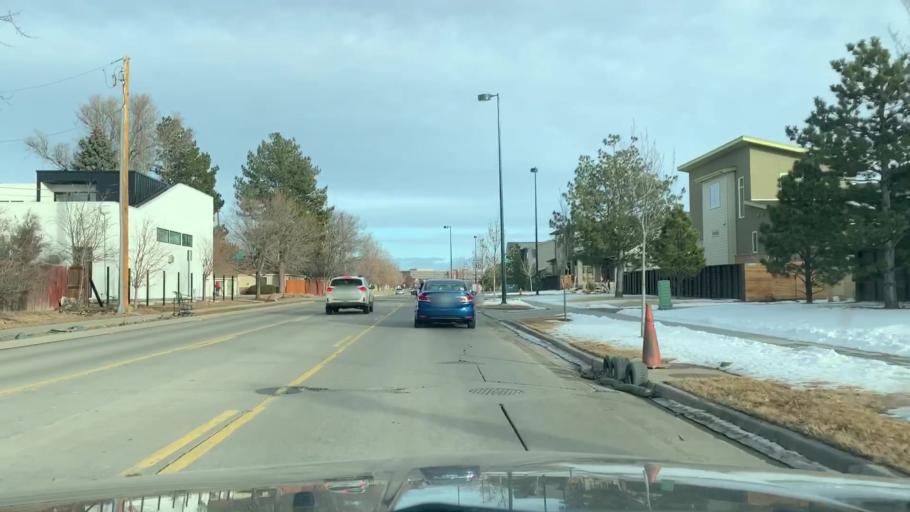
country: US
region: Colorado
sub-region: Arapahoe County
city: Glendale
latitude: 39.7183
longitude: -104.9096
